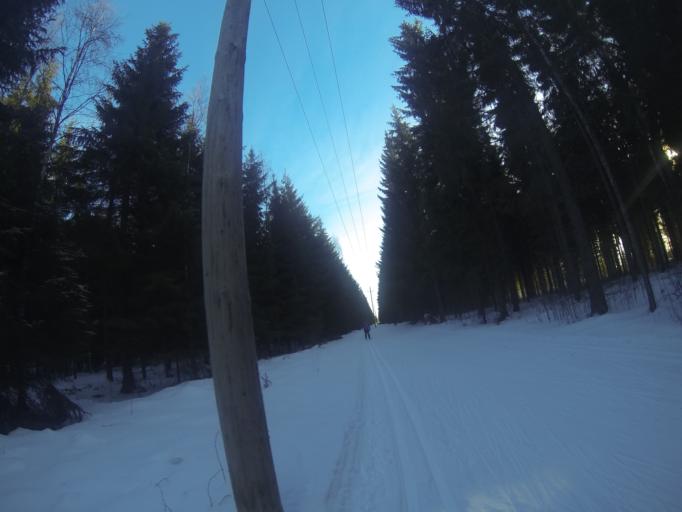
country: FI
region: Southern Savonia
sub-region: Savonlinna
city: Savonlinna
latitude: 61.9272
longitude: 28.8938
